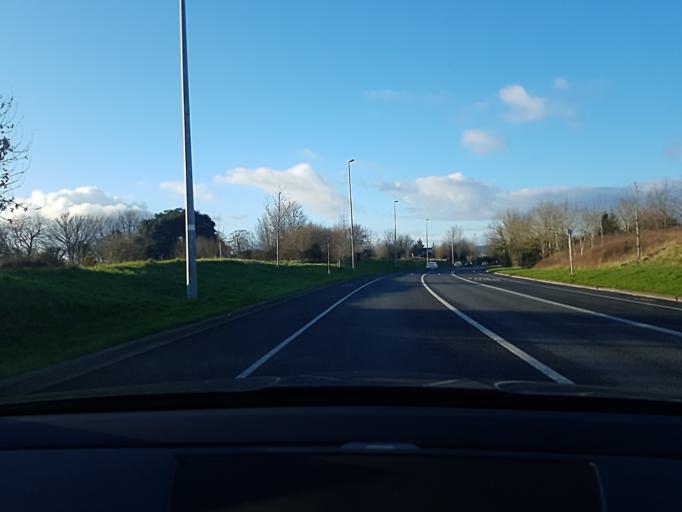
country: IE
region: Munster
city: Moyross
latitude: 52.6617
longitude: -8.6656
